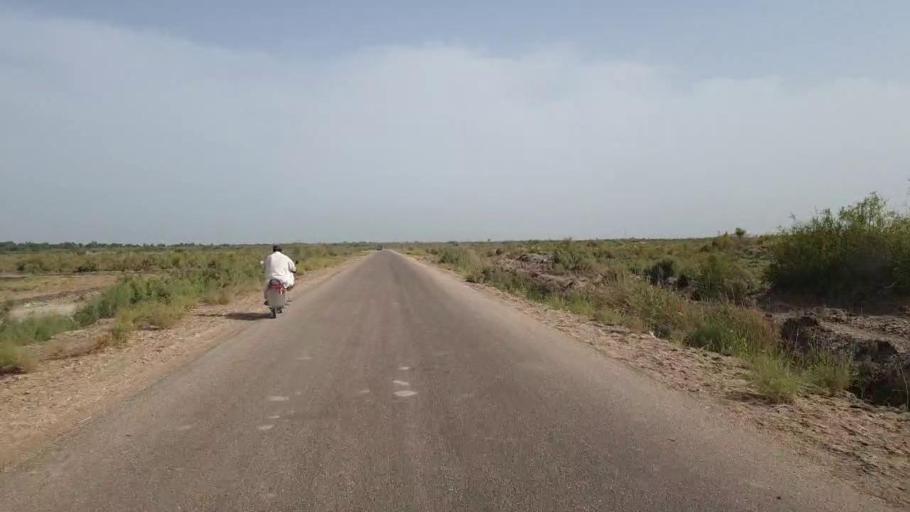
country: PK
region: Sindh
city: Sakrand
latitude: 26.2757
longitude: 68.2716
